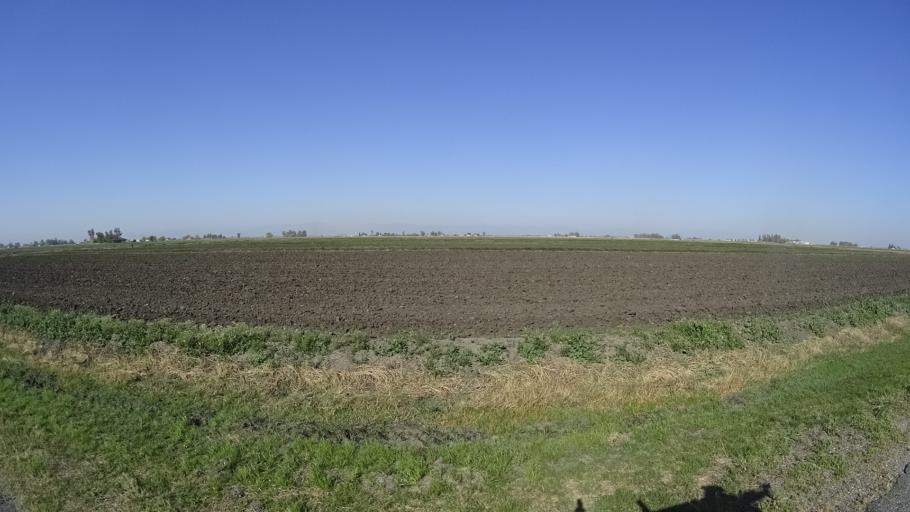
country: US
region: California
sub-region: Glenn County
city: Willows
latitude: 39.5630
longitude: -122.0838
